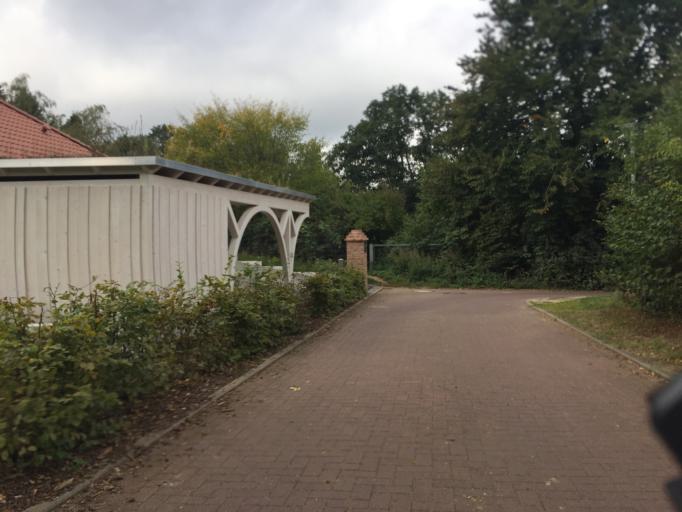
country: DE
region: Schleswig-Holstein
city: Munsterdorf
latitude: 53.9225
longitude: 9.5442
